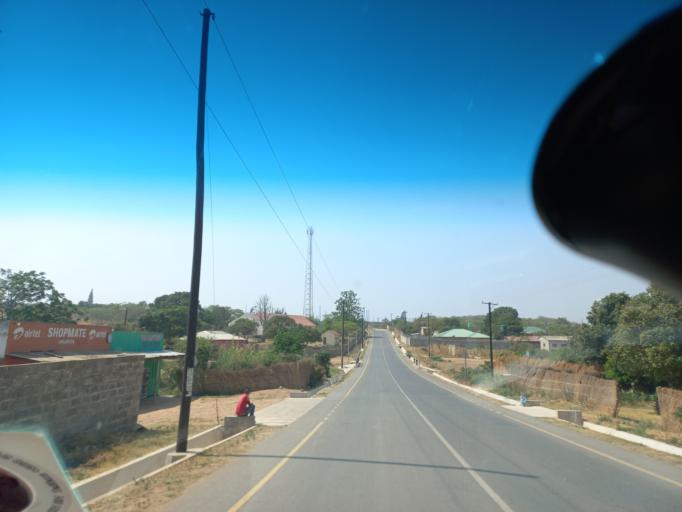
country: ZM
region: Lusaka
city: Lusaka
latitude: -15.5679
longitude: 28.2700
